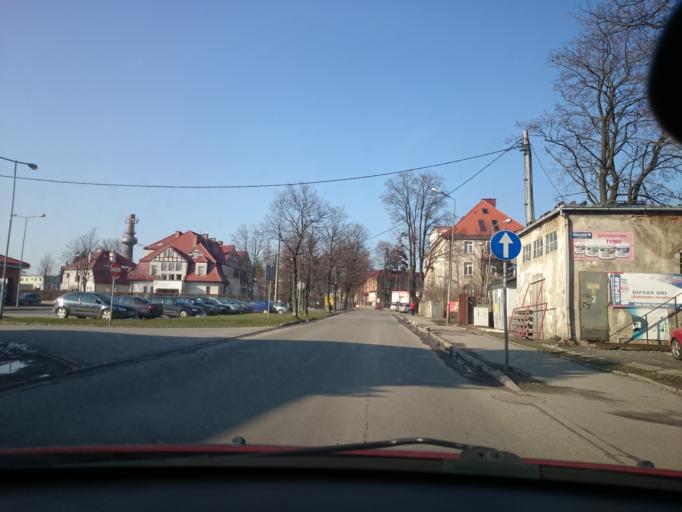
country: PL
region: Lower Silesian Voivodeship
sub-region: Powiat klodzki
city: Bystrzyca Klodzka
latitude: 50.2996
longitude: 16.6475
